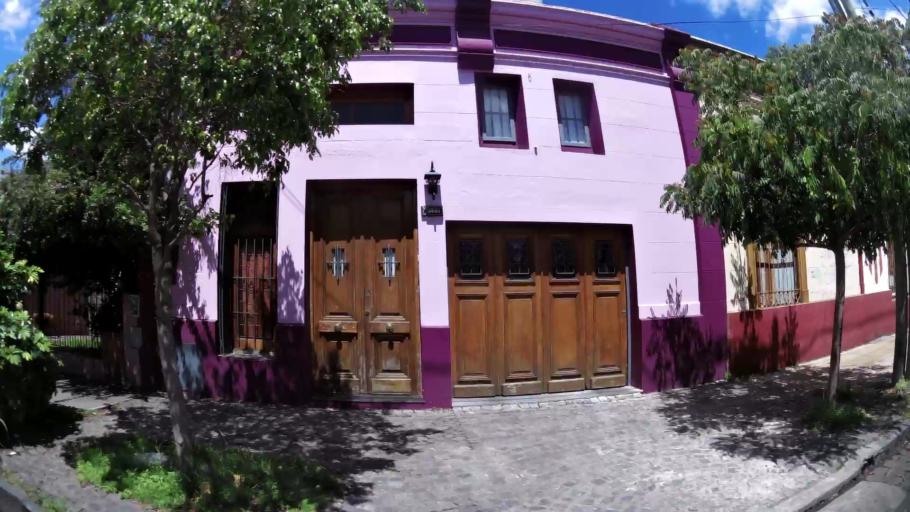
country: AR
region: Buenos Aires
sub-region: Partido de Lanus
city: Lanus
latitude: -34.7308
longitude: -58.3992
